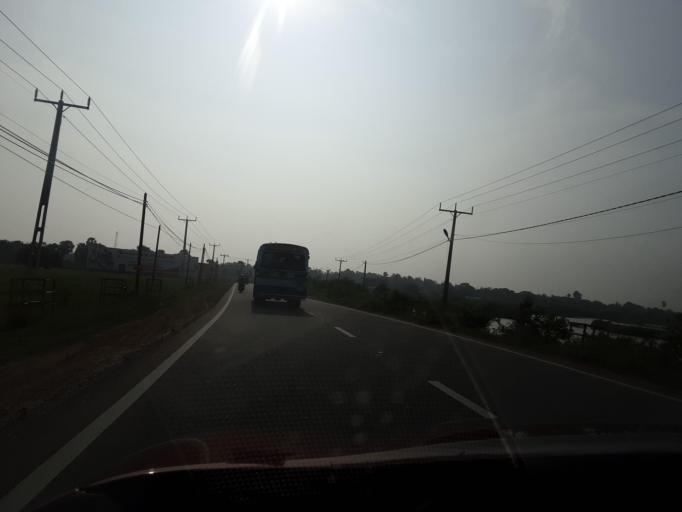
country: LK
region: Northern Province
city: Jaffna
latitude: 9.6614
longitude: 80.0599
